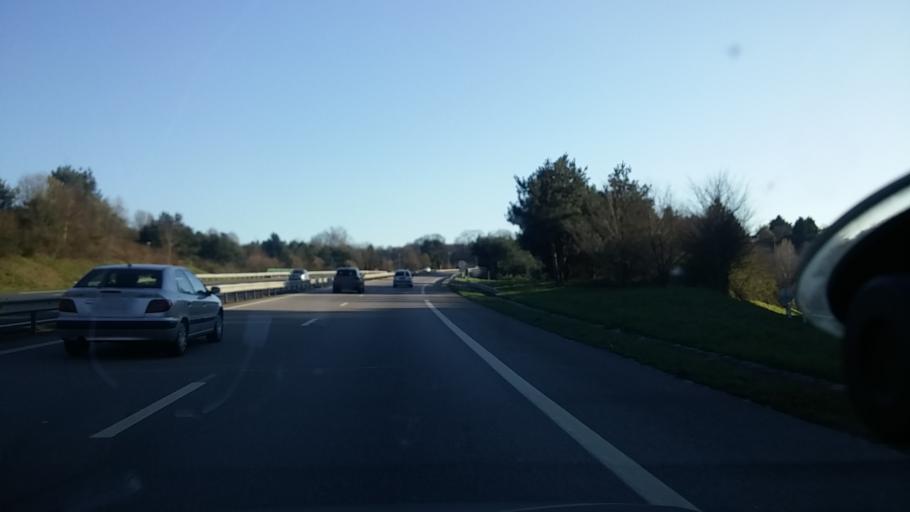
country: FR
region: Limousin
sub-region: Departement de la Haute-Vienne
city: Bessines-sur-Gartempe
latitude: 46.1125
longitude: 1.3754
